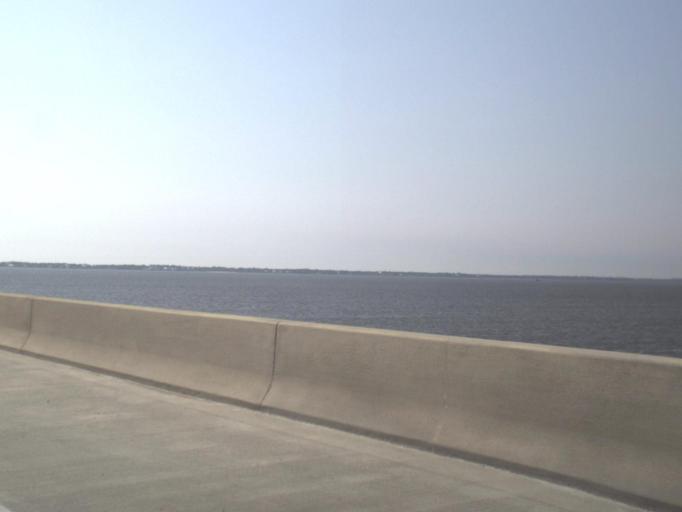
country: US
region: Florida
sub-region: Franklin County
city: Eastpoint
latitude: 29.6904
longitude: -84.8864
